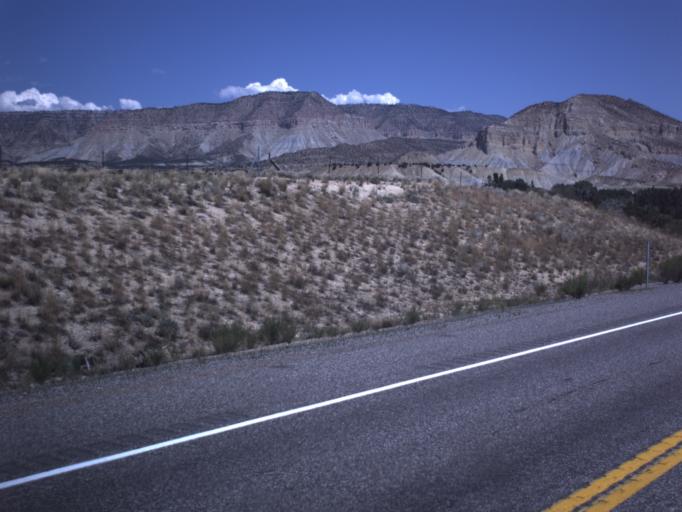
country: US
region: Utah
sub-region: Emery County
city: Ferron
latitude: 38.8980
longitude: -111.2764
